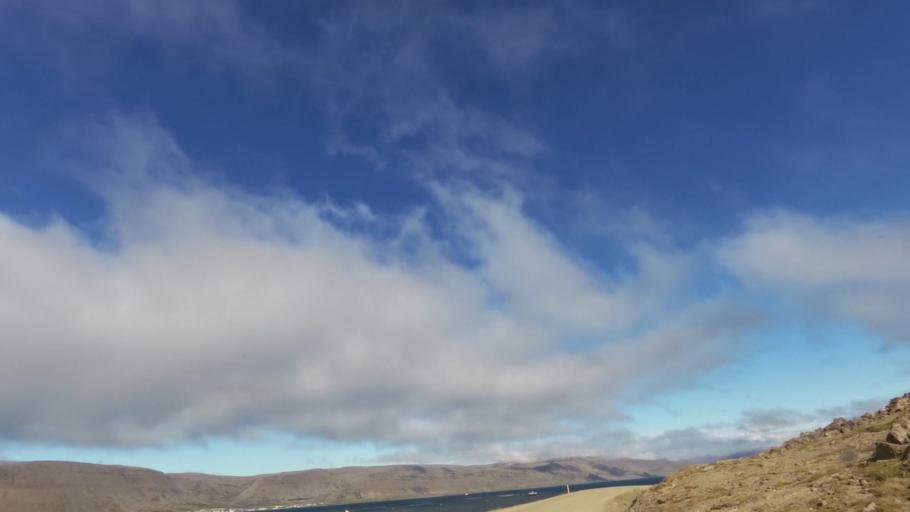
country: IS
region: West
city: Olafsvik
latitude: 65.5765
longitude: -24.0708
